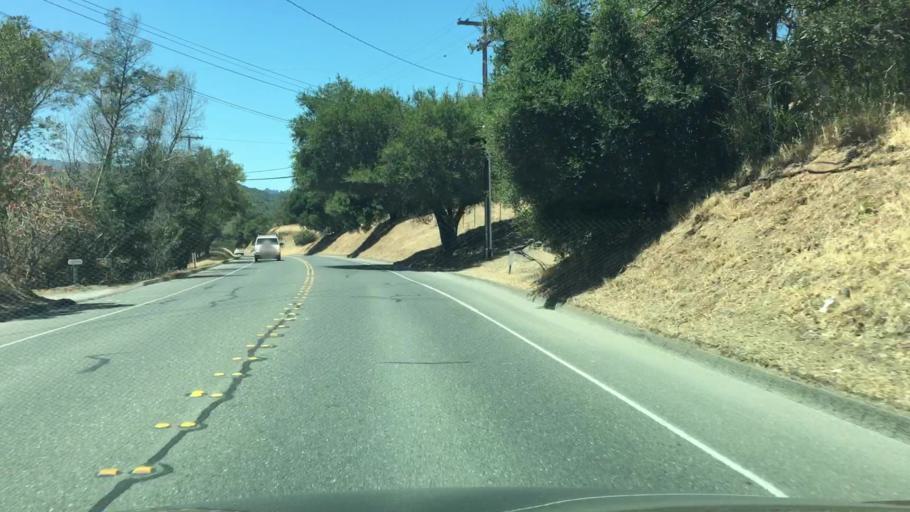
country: US
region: California
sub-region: San Mateo County
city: Emerald Lake Hills
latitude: 37.4750
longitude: -122.2672
